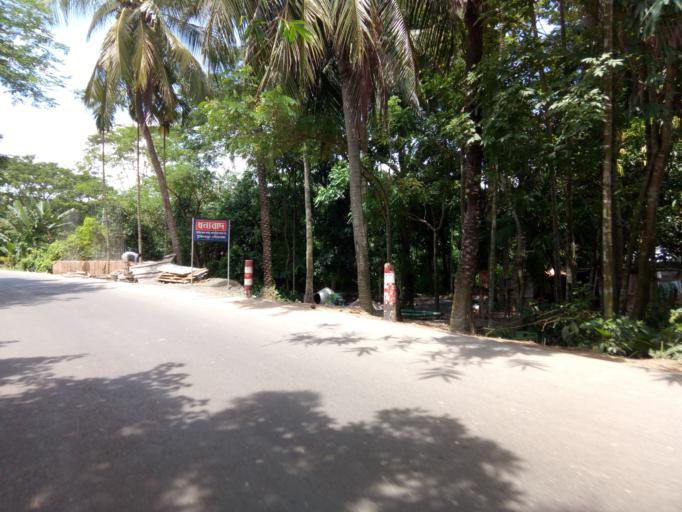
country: BD
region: Dhaka
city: Tungipara
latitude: 22.8995
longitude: 89.8883
